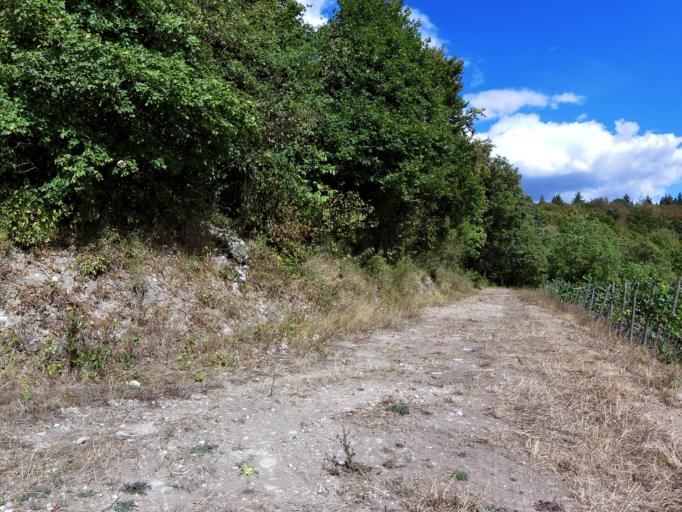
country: DE
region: Bavaria
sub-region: Regierungsbezirk Unterfranken
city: Margetshochheim
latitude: 49.8533
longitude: 9.8658
